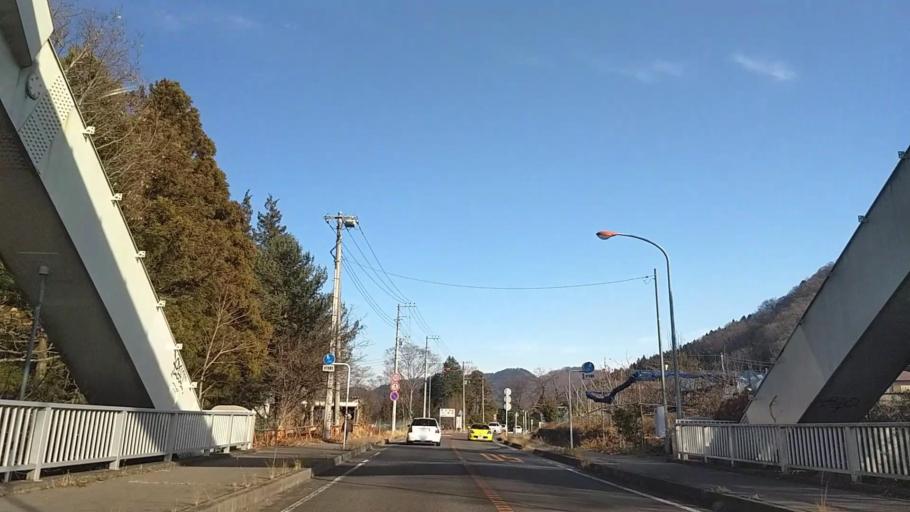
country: JP
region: Yamanashi
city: Uenohara
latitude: 35.5608
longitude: 139.1803
